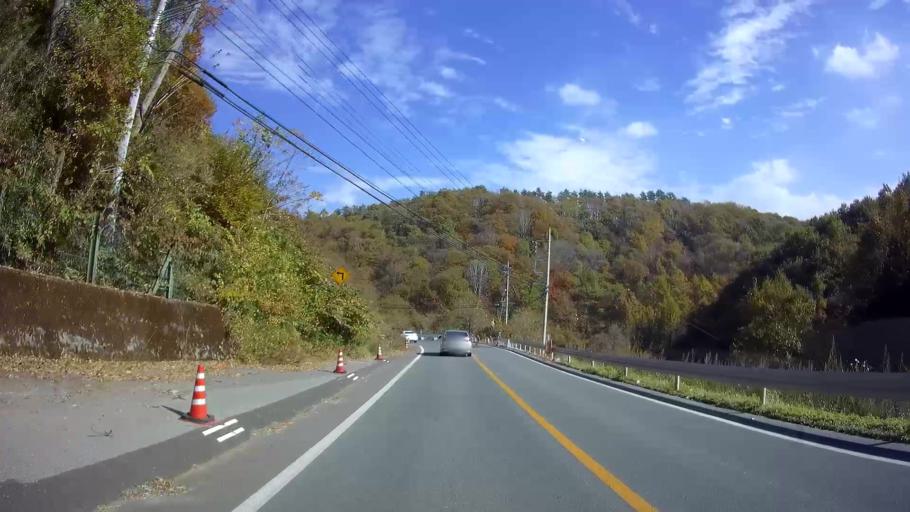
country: JP
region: Gunma
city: Nakanojomachi
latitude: 36.4953
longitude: 138.7762
